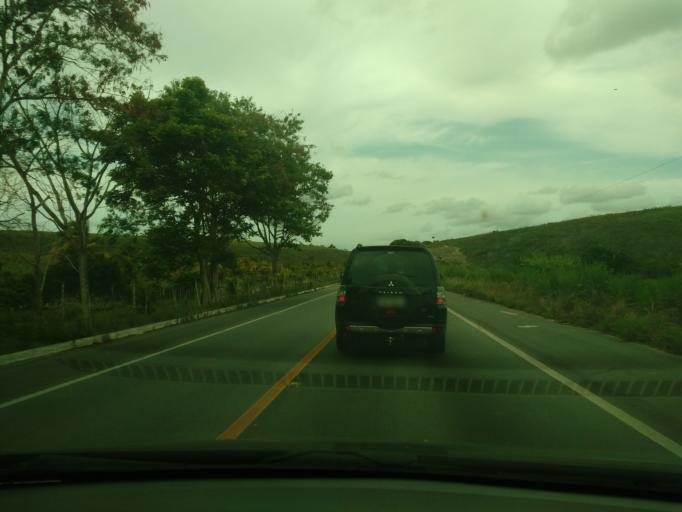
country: BR
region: Alagoas
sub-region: Messias
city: Messias
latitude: -9.3691
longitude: -35.8424
